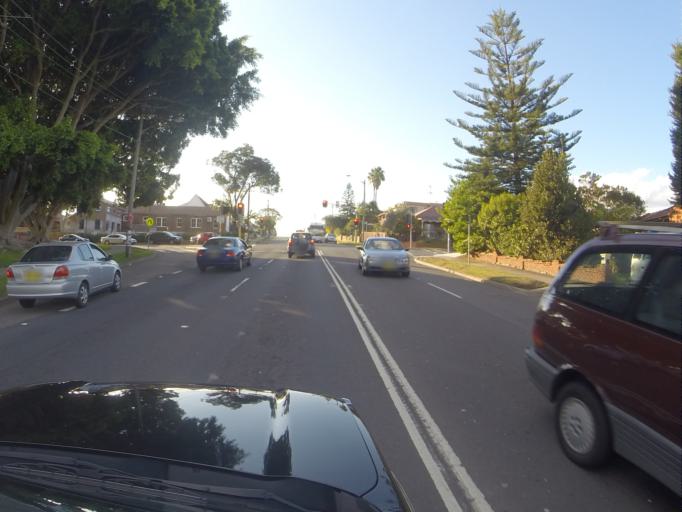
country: AU
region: New South Wales
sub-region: Rockdale
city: Bexley North
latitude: -33.9331
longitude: 151.1101
